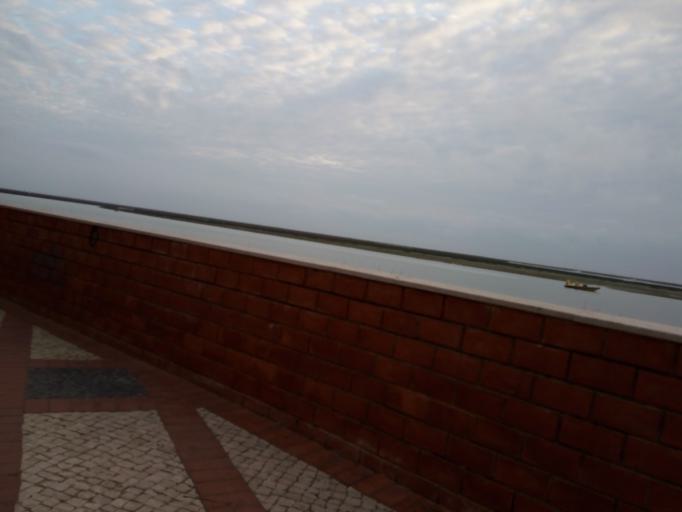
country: PT
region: Faro
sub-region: Faro
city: Faro
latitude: 37.0116
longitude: -7.9347
